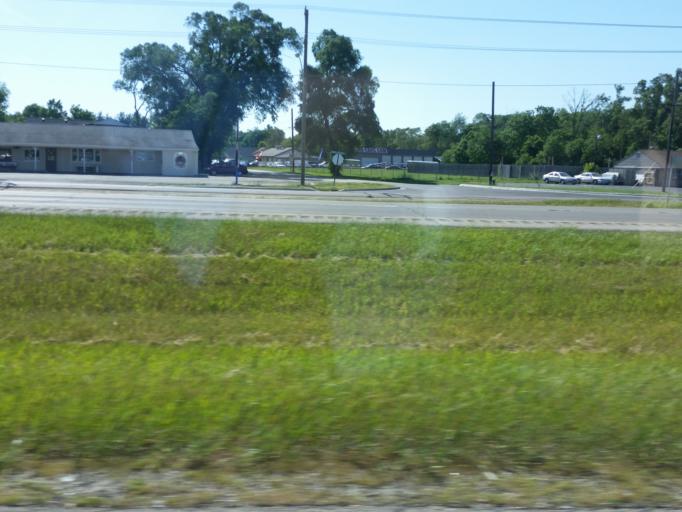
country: US
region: Illinois
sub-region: Winnebago County
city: Roscoe
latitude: 42.3855
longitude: -89.0193
